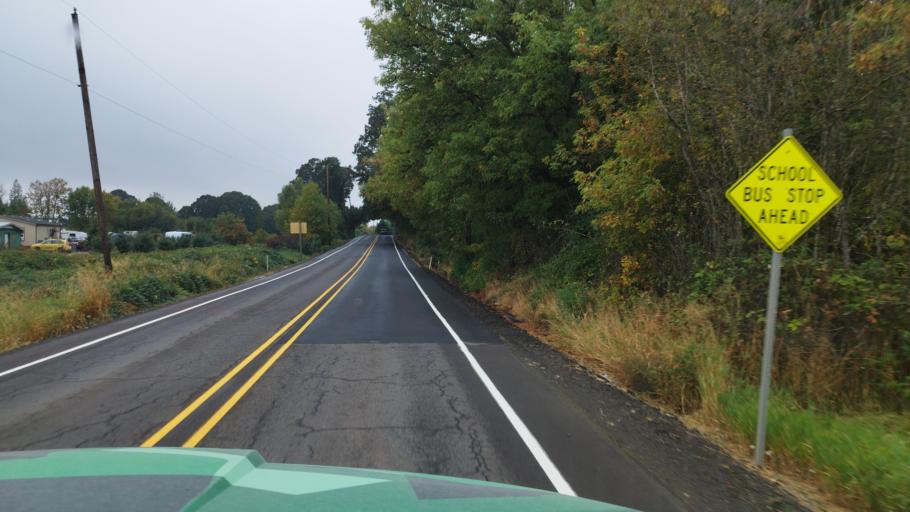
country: US
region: Oregon
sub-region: Yamhill County
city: Yamhill
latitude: 45.3492
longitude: -123.1758
